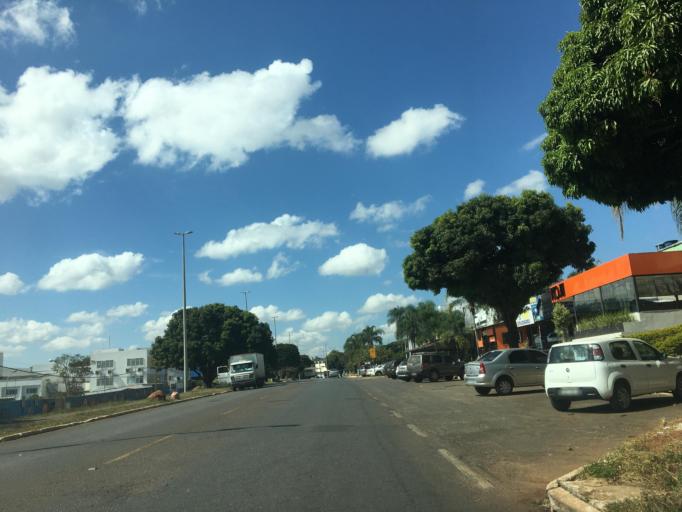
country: BR
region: Federal District
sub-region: Brasilia
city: Brasilia
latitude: -15.6458
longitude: -47.7892
